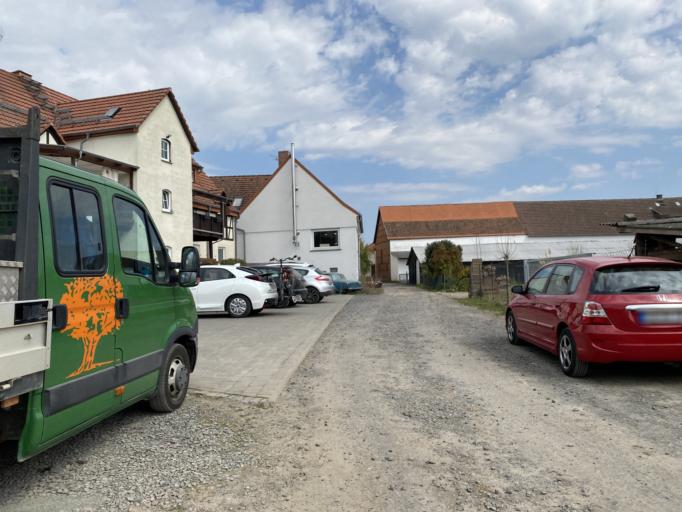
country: DE
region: Hesse
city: Budingen
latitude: 50.2527
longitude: 9.0714
